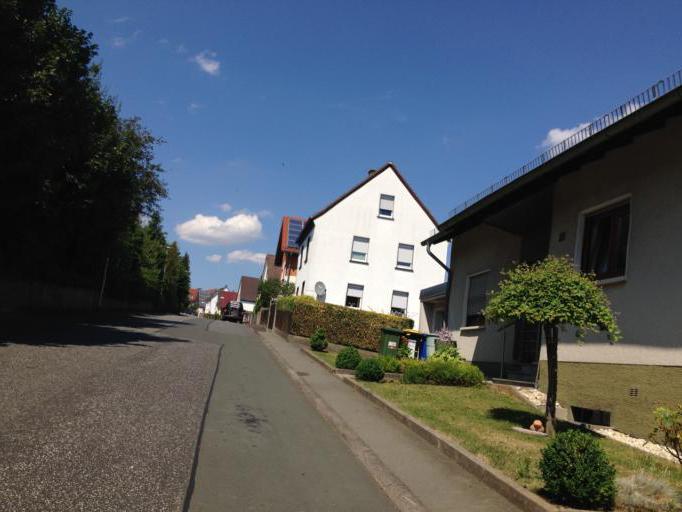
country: DE
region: Hesse
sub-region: Regierungsbezirk Giessen
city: Heuchelheim
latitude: 50.6126
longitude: 8.6388
